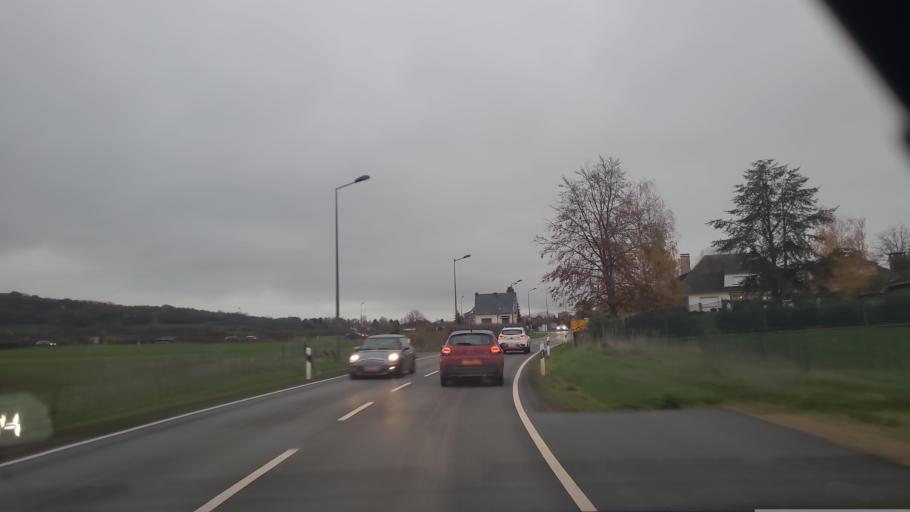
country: LU
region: Luxembourg
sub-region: Canton de Capellen
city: Bascharage
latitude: 49.5708
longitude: 5.8991
